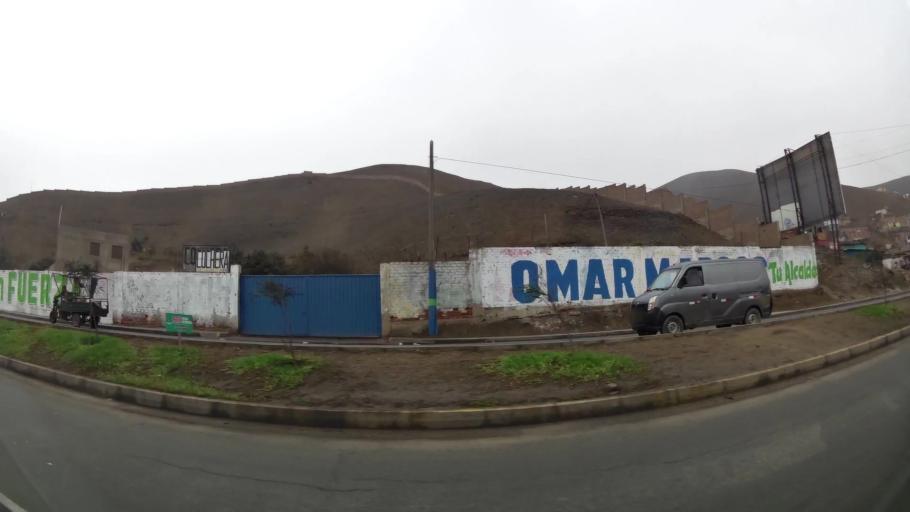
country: PE
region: Lima
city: Ventanilla
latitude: -11.8899
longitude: -77.1260
